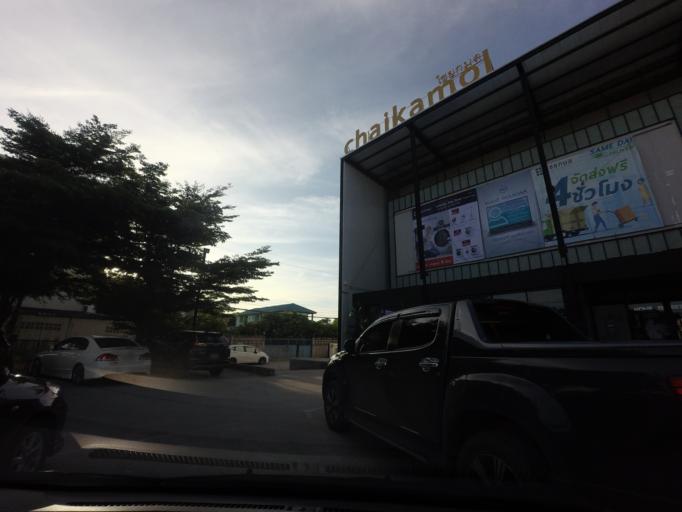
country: TH
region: Chon Buri
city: Sattahip
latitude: 12.6730
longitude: 100.8996
